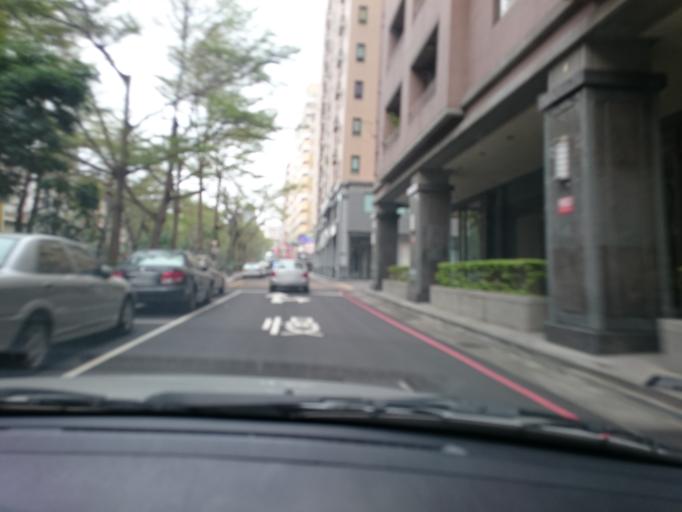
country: TW
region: Taiwan
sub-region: Taichung City
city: Taichung
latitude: 24.1728
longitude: 120.6407
